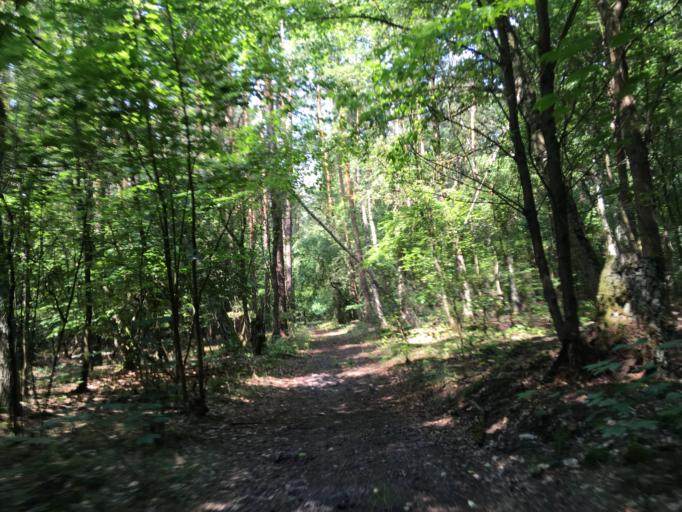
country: DE
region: Brandenburg
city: Glienicke
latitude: 52.6798
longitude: 13.3580
